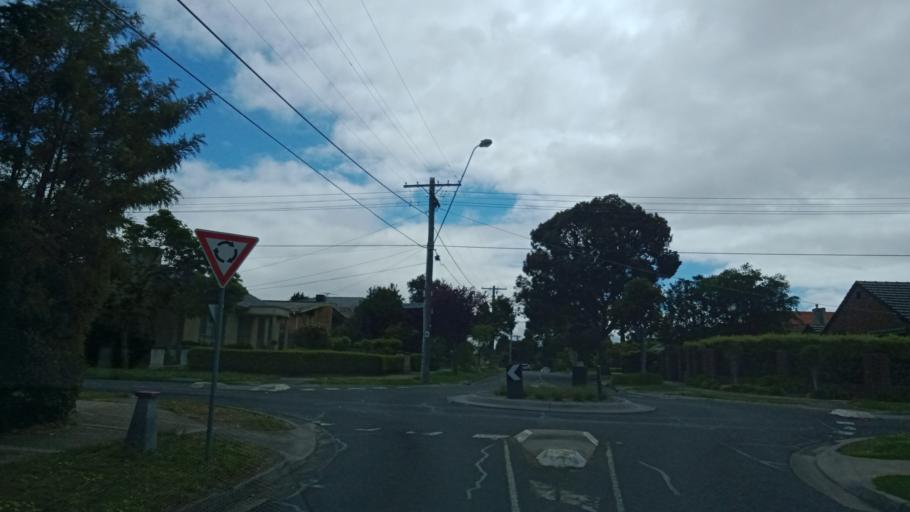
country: AU
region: Victoria
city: Burwood East
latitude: -37.8650
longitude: 145.1363
